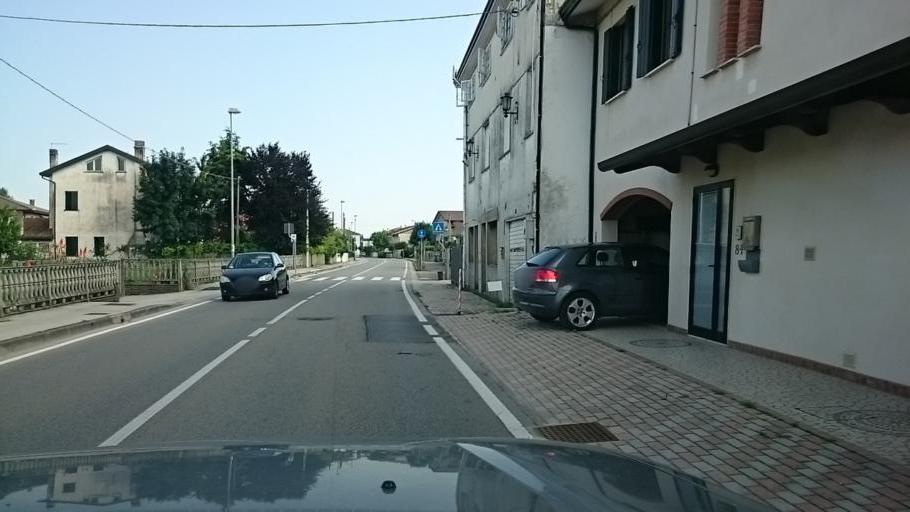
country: IT
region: Veneto
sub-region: Provincia di Padova
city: Saletto
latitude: 45.4795
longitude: 11.8550
